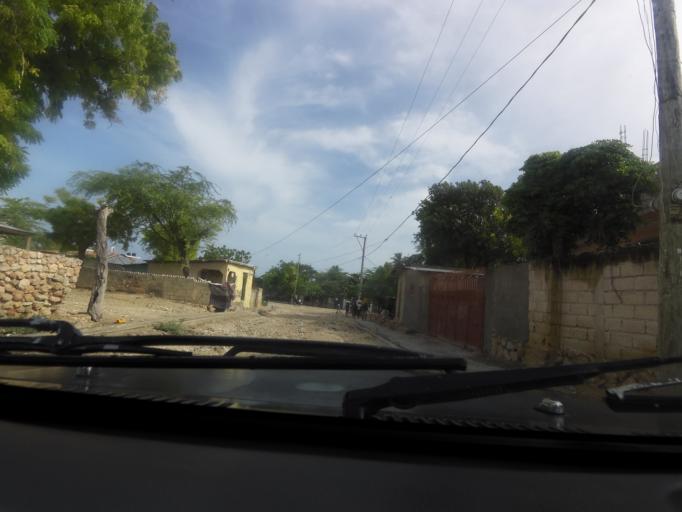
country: HT
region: Ouest
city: Anse a Galets
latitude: 18.8364
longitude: -72.8633
